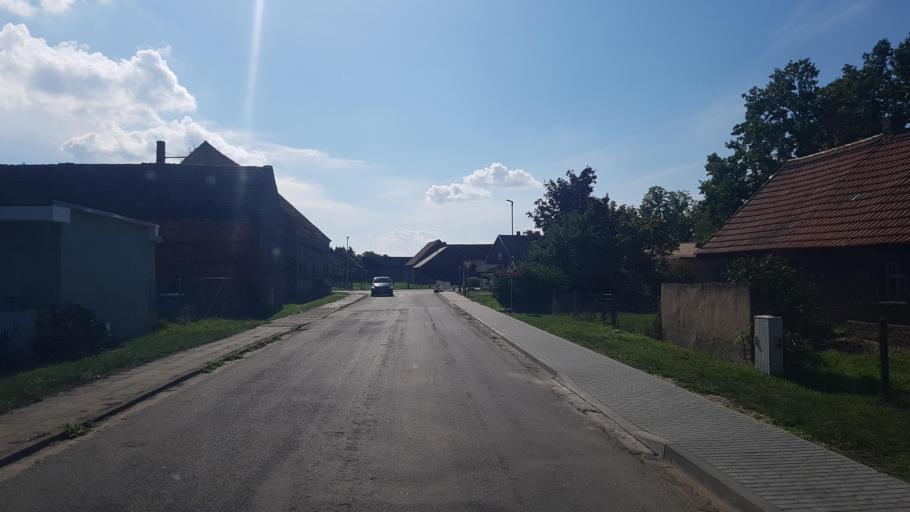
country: DE
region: Brandenburg
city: Ihlow
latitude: 51.8332
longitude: 13.3474
